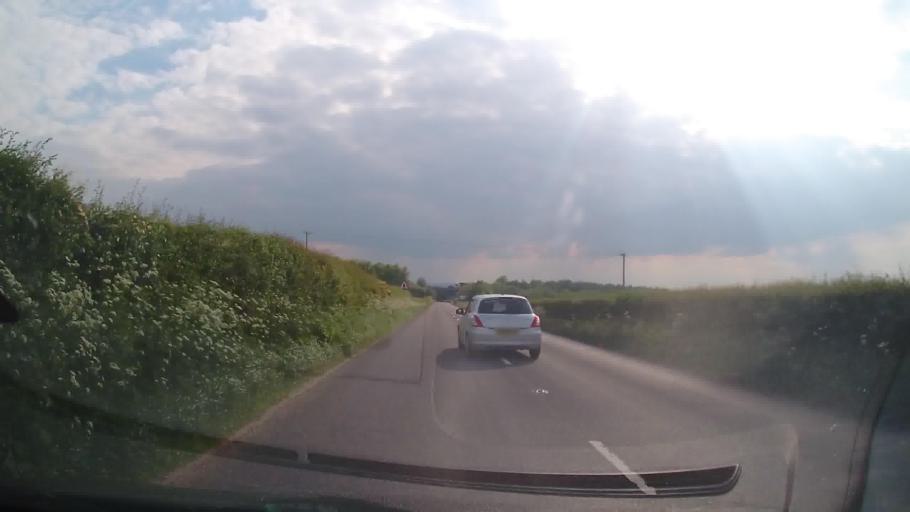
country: GB
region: England
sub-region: Shropshire
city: Withington
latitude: 52.6911
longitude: -2.5876
